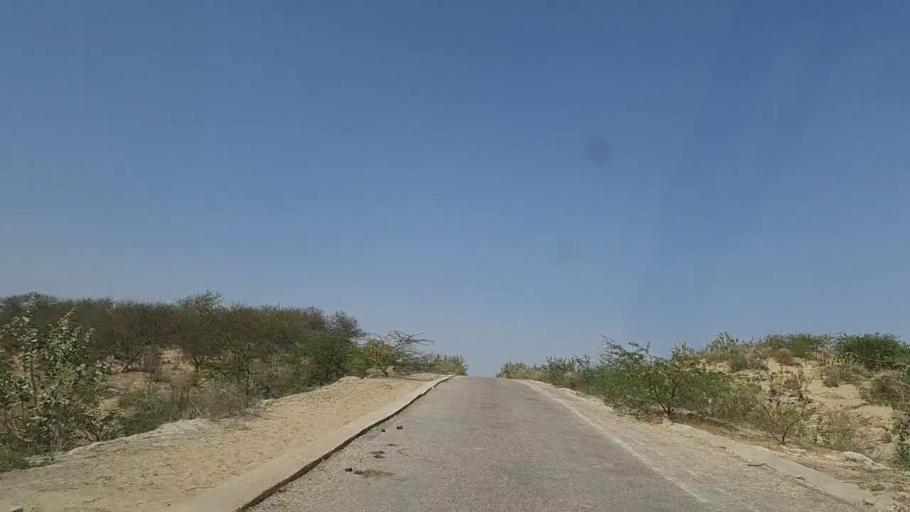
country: PK
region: Sindh
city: Diplo
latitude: 24.5817
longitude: 69.3197
